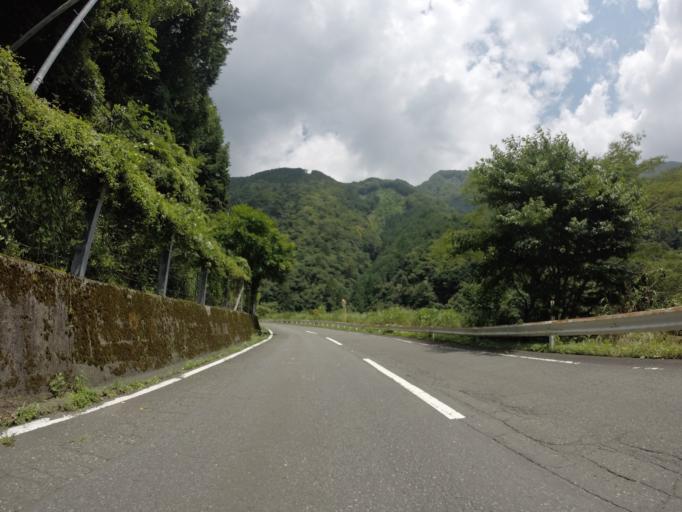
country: JP
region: Shizuoka
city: Fujinomiya
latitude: 35.2865
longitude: 138.3417
